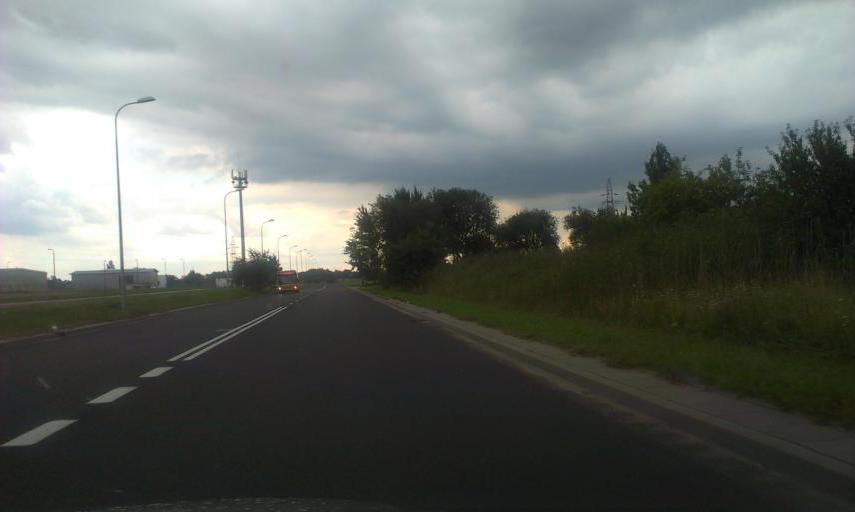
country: PL
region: West Pomeranian Voivodeship
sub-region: Koszalin
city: Koszalin
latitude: 54.1913
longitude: 16.1457
